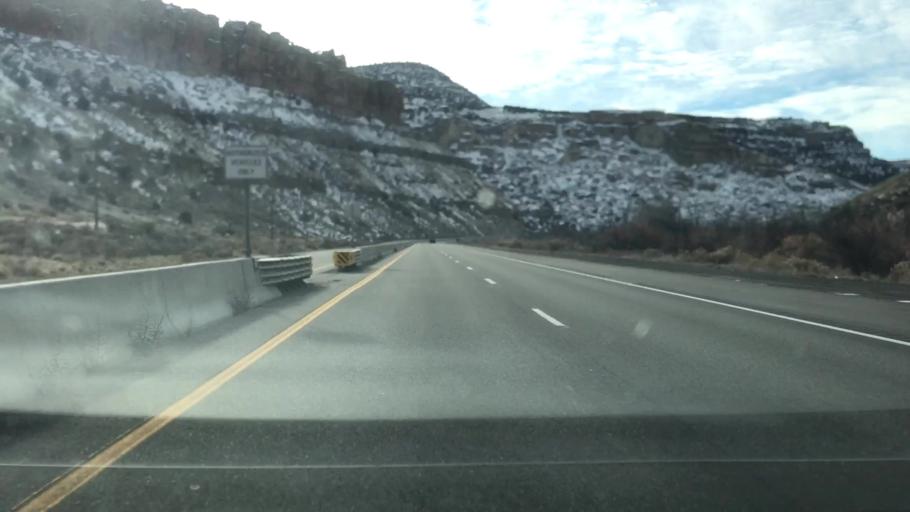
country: US
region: Colorado
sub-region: Mesa County
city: Palisade
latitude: 39.2147
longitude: -108.2564
